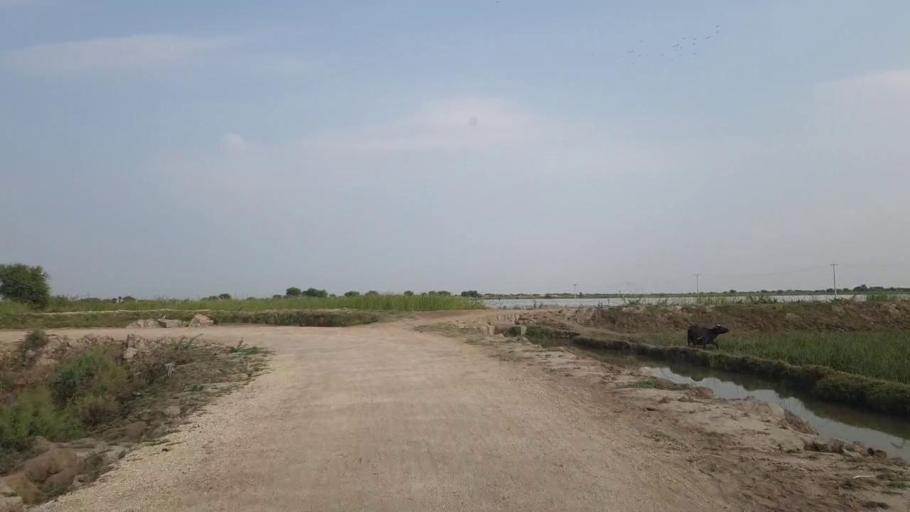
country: PK
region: Sindh
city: Kadhan
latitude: 24.4585
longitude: 68.8054
